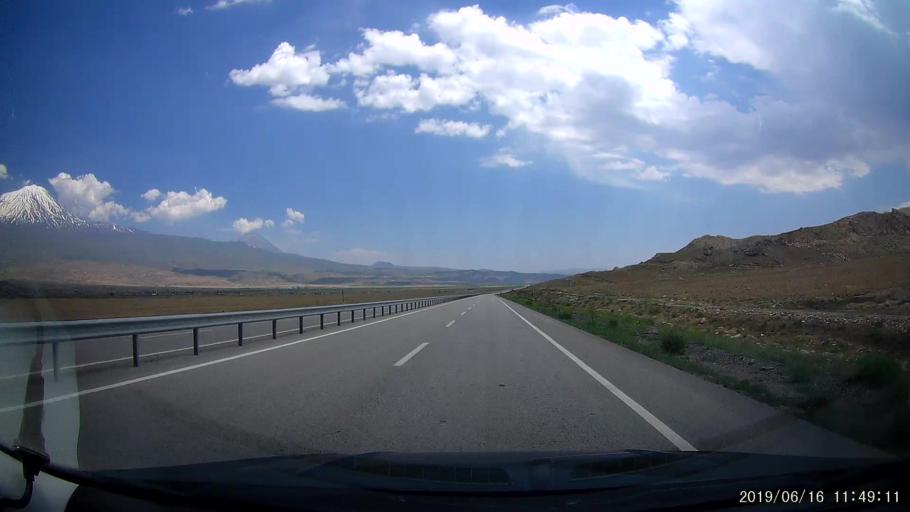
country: TR
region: Agri
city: Dogubayazit
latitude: 39.5575
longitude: 44.1587
